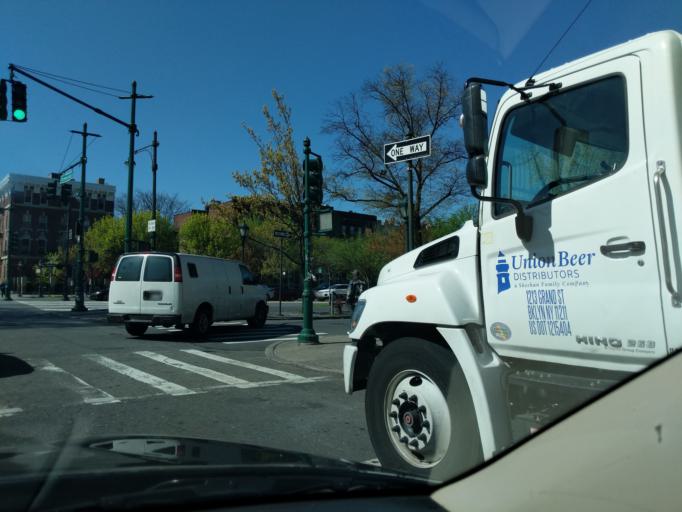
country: US
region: New York
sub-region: Kings County
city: Brooklyn
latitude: 40.6693
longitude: -73.9339
